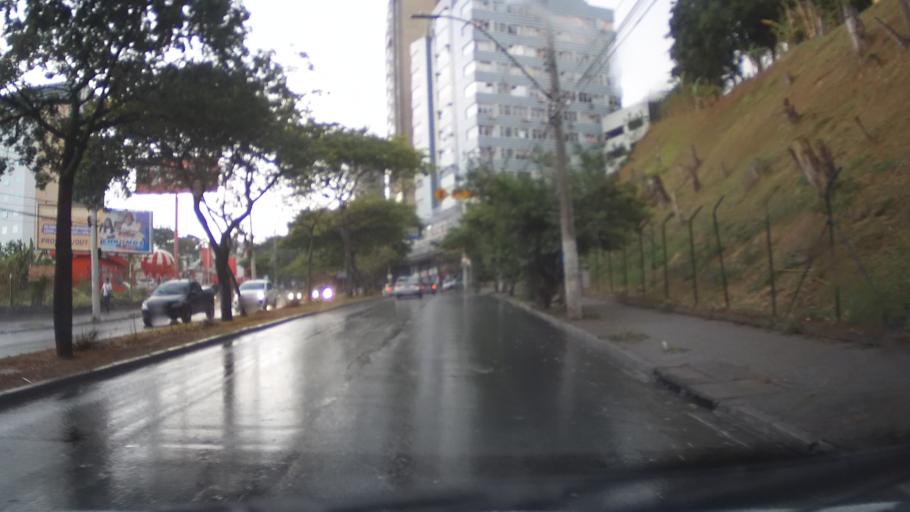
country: BR
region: Minas Gerais
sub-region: Belo Horizonte
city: Belo Horizonte
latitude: -19.9423
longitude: -43.9551
